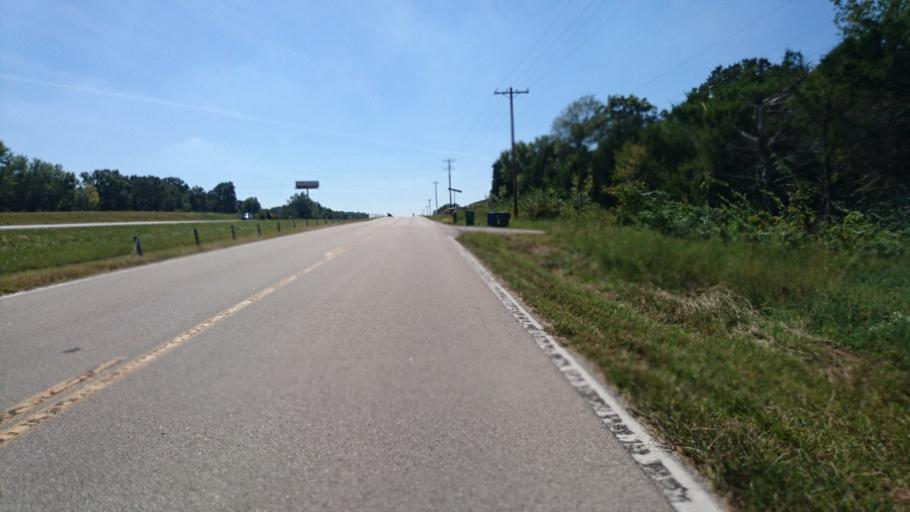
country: US
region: Missouri
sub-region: Franklin County
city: Sullivan
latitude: 38.2454
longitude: -91.1388
